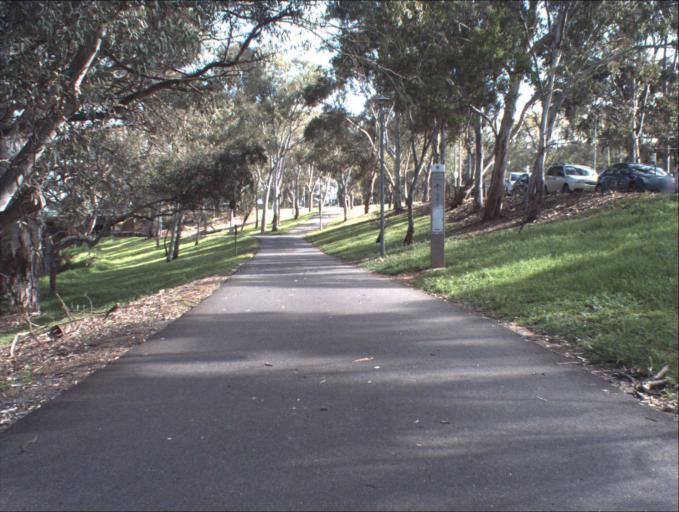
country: AU
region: South Australia
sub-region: Port Adelaide Enfield
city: Klemzig
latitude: -34.8868
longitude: 138.6401
